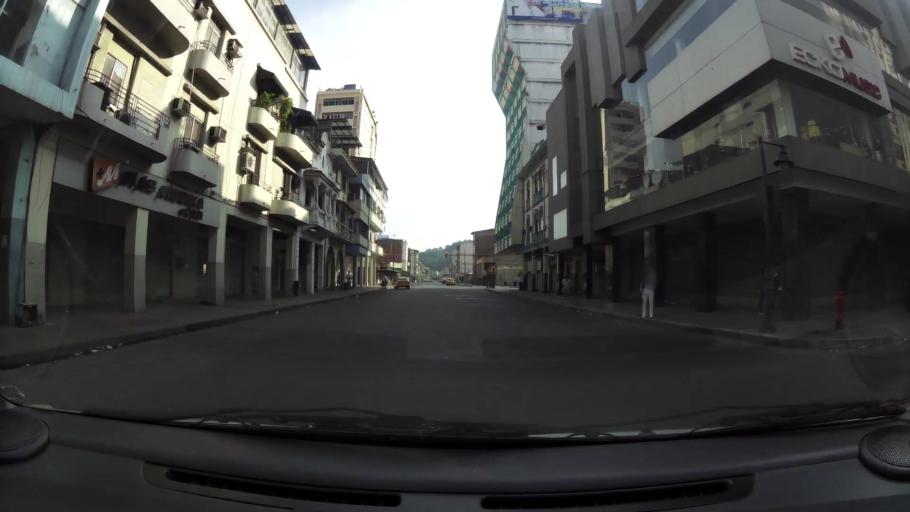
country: EC
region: Guayas
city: Guayaquil
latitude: -2.1899
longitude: -79.8860
